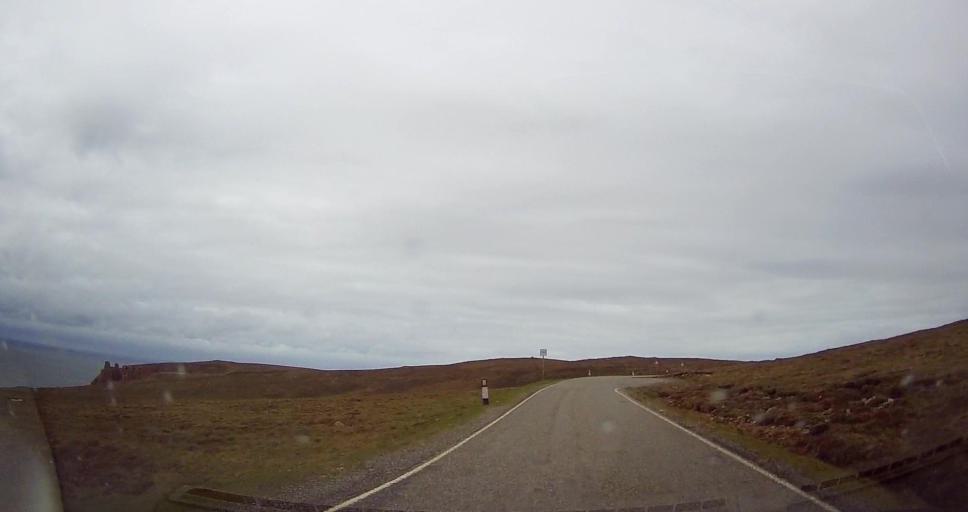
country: GB
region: Scotland
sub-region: Shetland Islands
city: Lerwick
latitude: 60.4853
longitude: -1.5203
